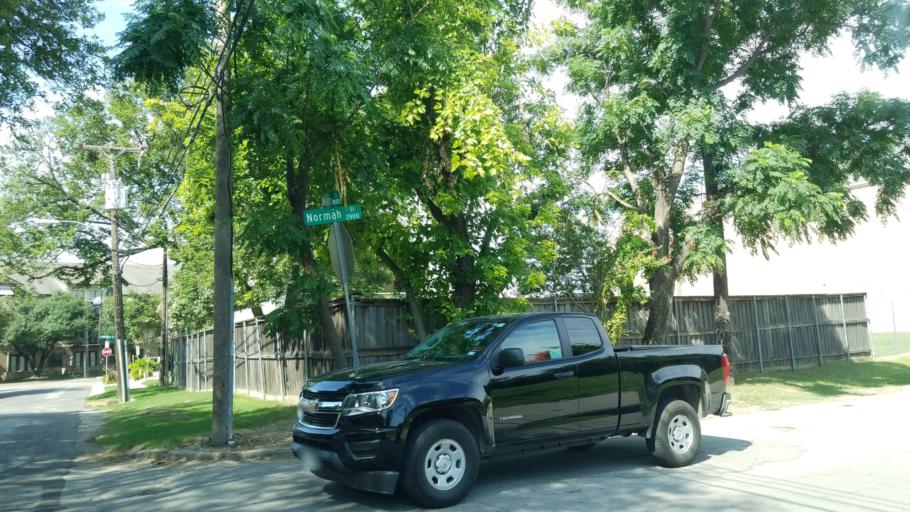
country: US
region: Texas
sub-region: Dallas County
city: Highland Park
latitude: 32.8160
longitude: -96.7872
